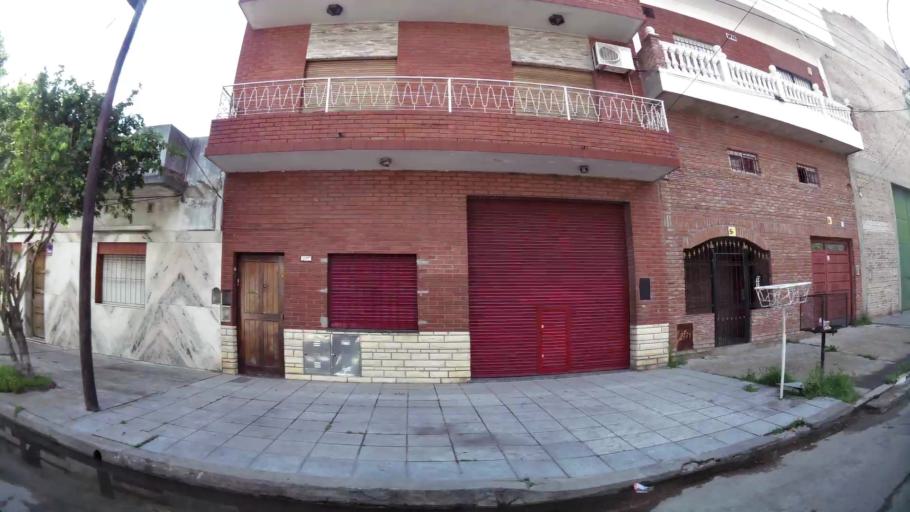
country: AR
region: Buenos Aires
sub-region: Partido de Lanus
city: Lanus
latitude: -34.6805
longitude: -58.4156
